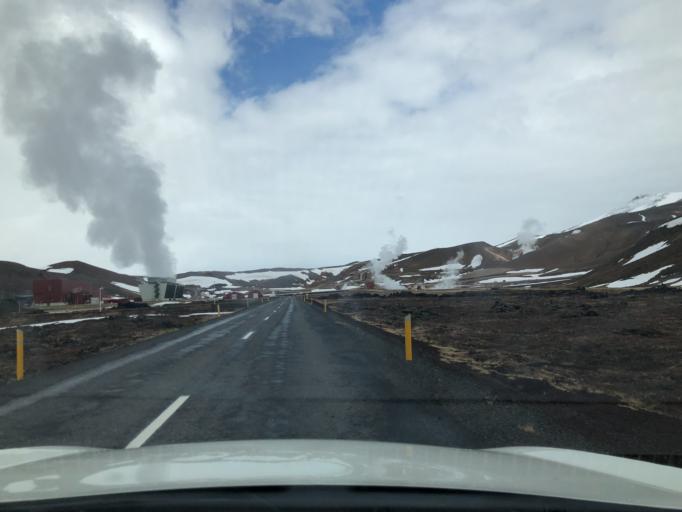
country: IS
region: Northeast
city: Laugar
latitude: 65.6982
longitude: -16.7734
